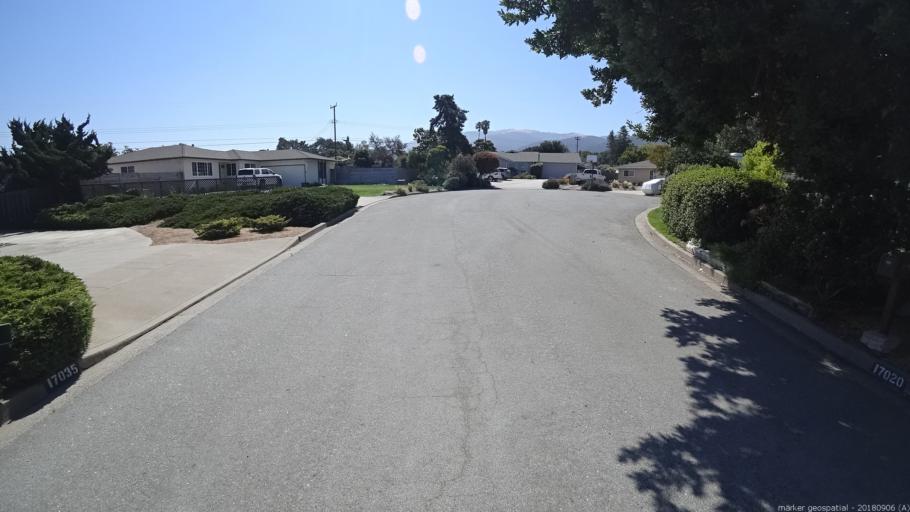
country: US
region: California
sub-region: Monterey County
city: Salinas
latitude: 36.5966
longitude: -121.6327
